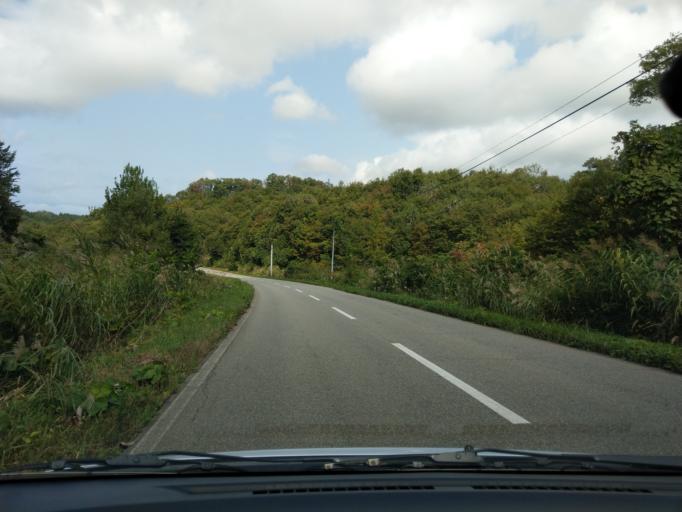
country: JP
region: Akita
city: Omagari
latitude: 39.4915
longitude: 140.3137
